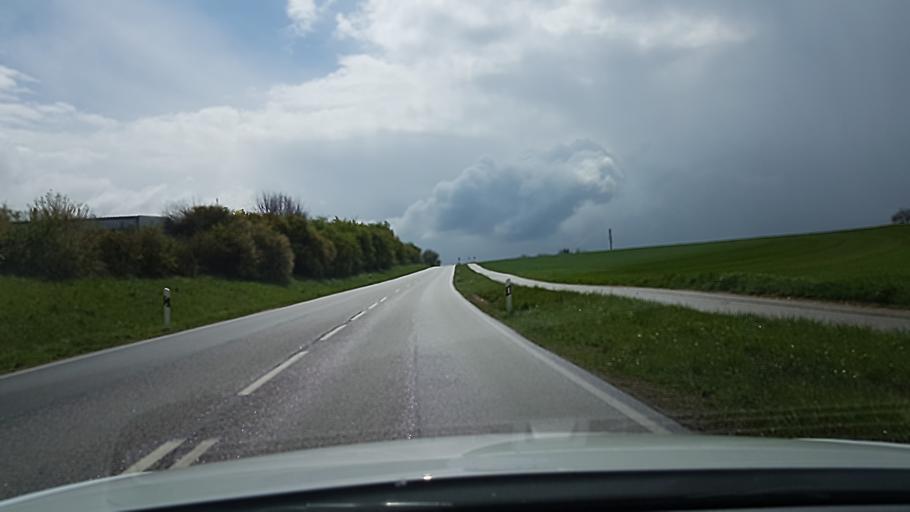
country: DE
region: Baden-Wuerttemberg
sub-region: Regierungsbezirk Stuttgart
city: Aspach
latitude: 48.9710
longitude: 9.3865
